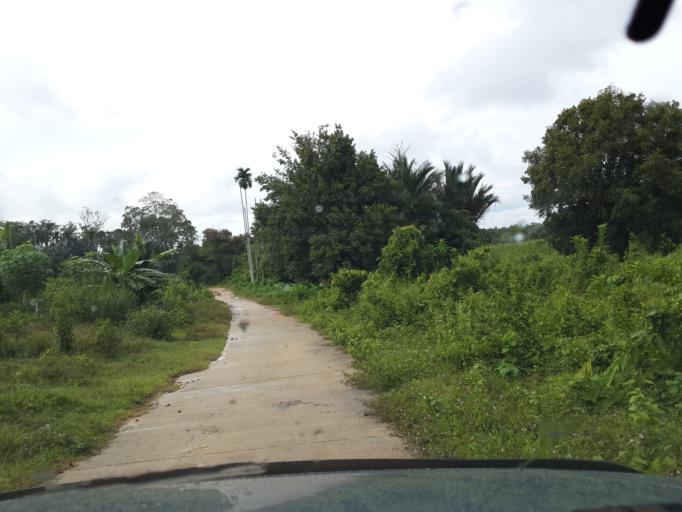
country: TH
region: Narathiwat
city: Rueso
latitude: 6.3812
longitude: 101.5242
